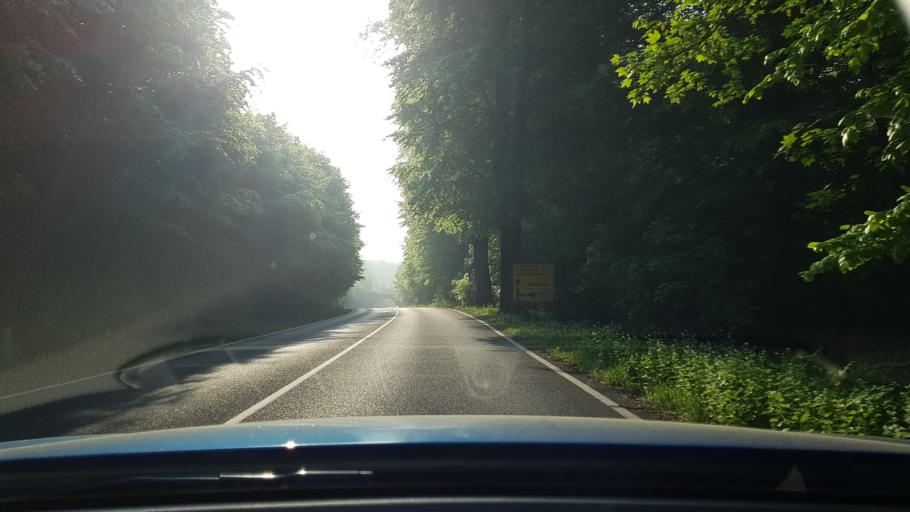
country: LU
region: Luxembourg
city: Heisdorf-sur-Alzette
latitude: 49.6595
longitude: 6.1898
